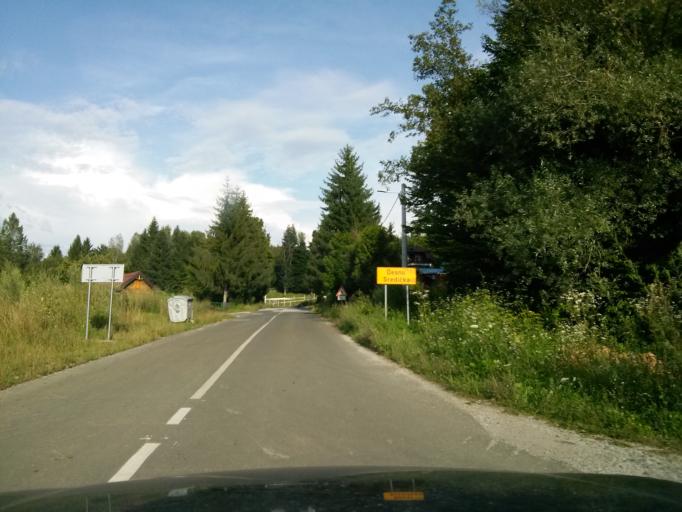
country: HR
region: Sisacko-Moslavacka
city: Gvozd
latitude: 45.5259
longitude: 15.8750
